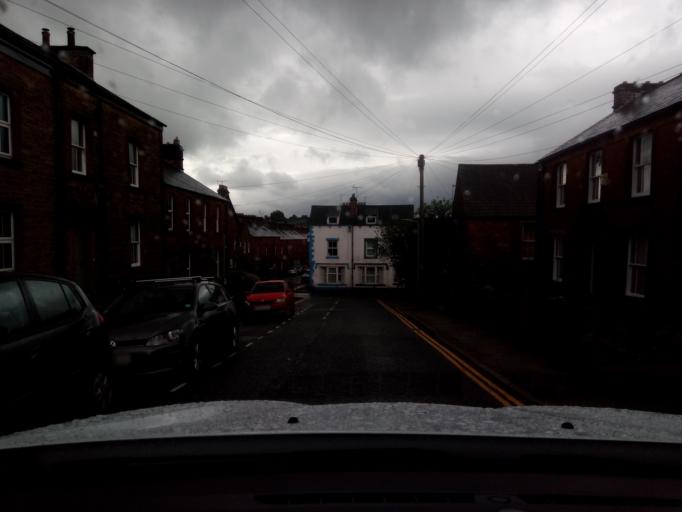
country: GB
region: England
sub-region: Cumbria
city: Penrith
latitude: 54.6672
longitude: -2.7514
